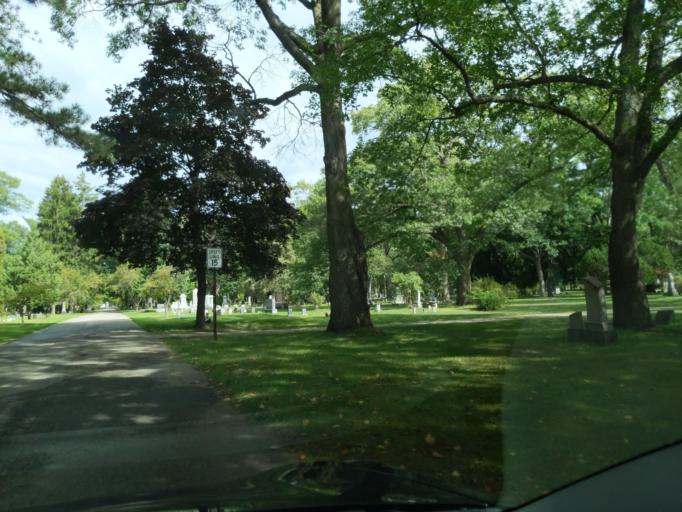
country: US
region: Michigan
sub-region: Grand Traverse County
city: Traverse City
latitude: 44.7554
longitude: -85.5891
